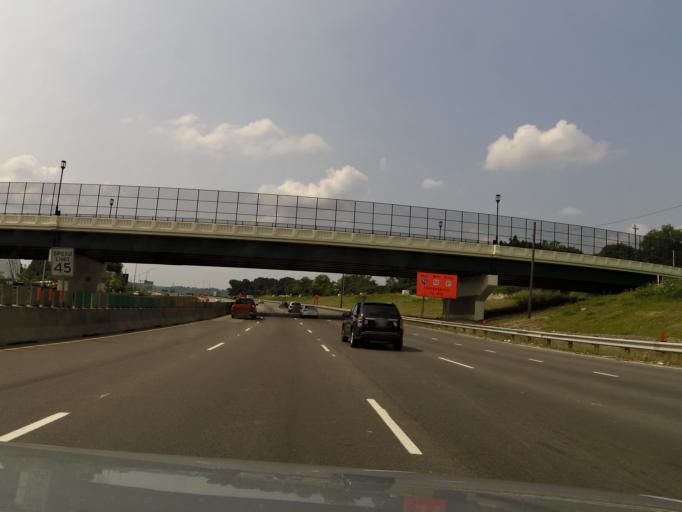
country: US
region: Ohio
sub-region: Hamilton County
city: Saint Bernard
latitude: 39.1424
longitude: -84.5351
